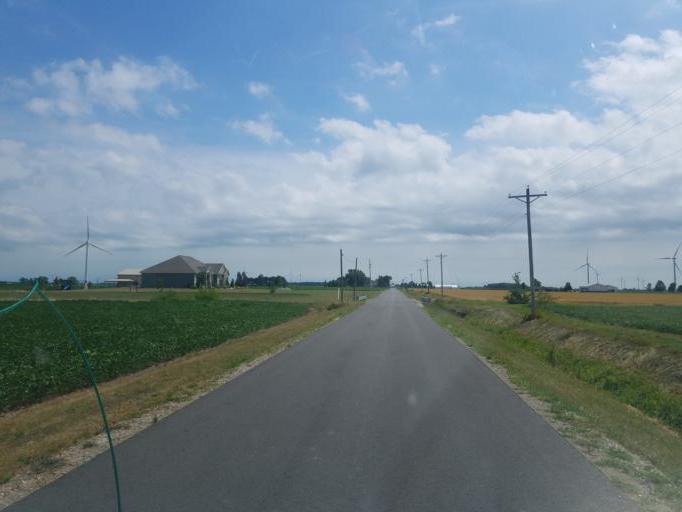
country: US
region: Ohio
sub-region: Paulding County
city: Payne
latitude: 41.1049
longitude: -84.7652
